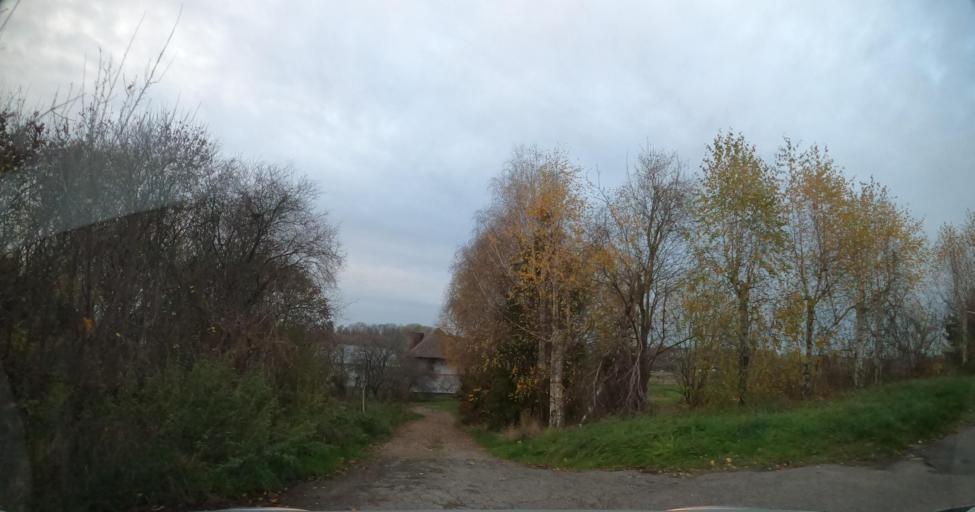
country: PL
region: West Pomeranian Voivodeship
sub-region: Powiat lobeski
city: Resko
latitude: 53.7750
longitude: 15.4155
